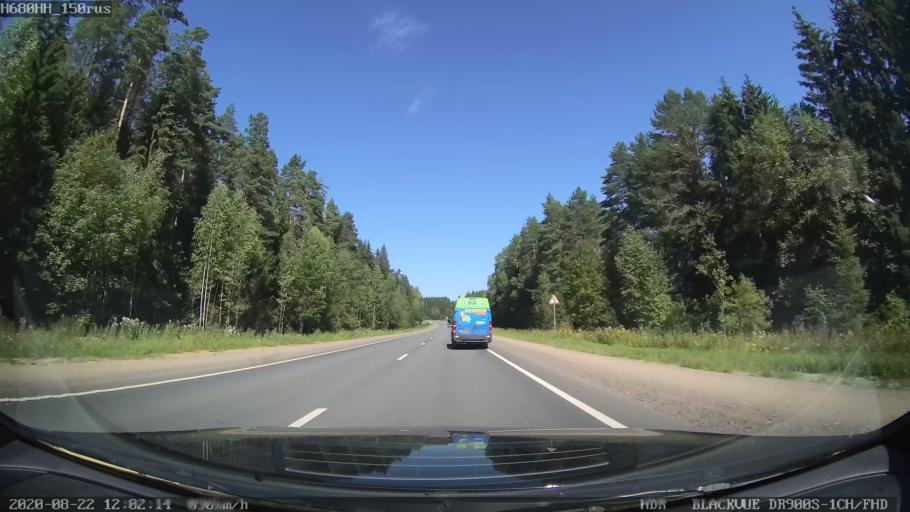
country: RU
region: Tverskaya
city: Rameshki
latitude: 57.2399
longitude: 36.1001
